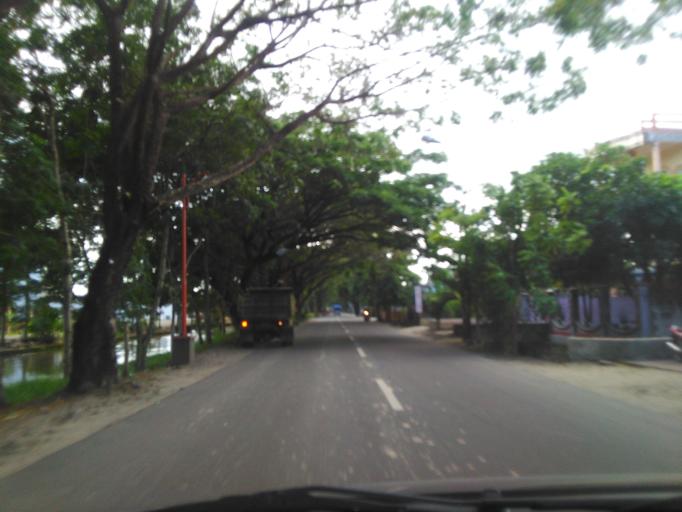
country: ID
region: South Sulawesi
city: Pinrang
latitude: -3.8064
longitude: 119.6454
